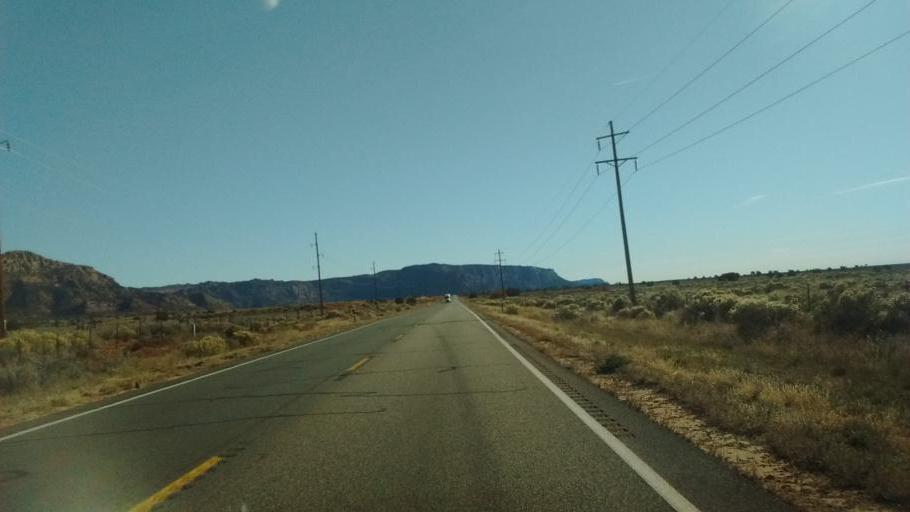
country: US
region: Arizona
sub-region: Mohave County
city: Colorado City
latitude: 37.0162
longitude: -113.0270
